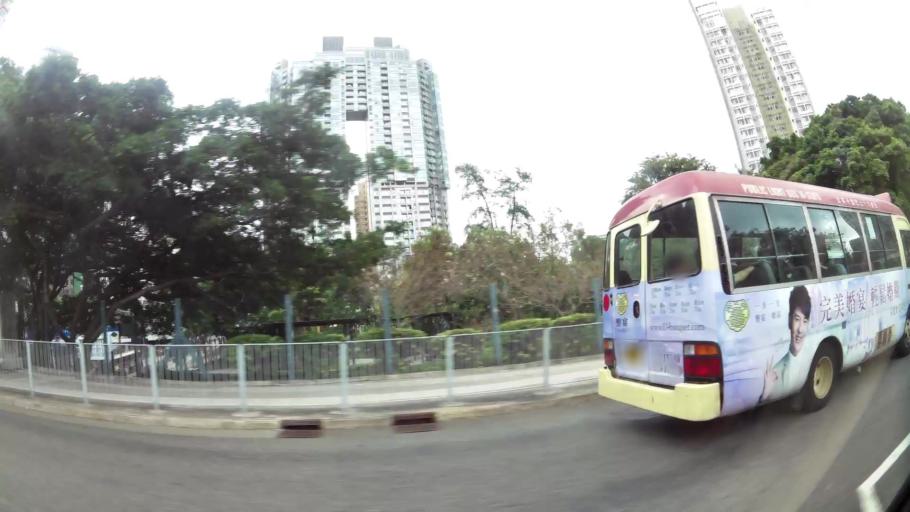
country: HK
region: Kowloon City
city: Kowloon
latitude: 22.3097
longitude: 114.1851
